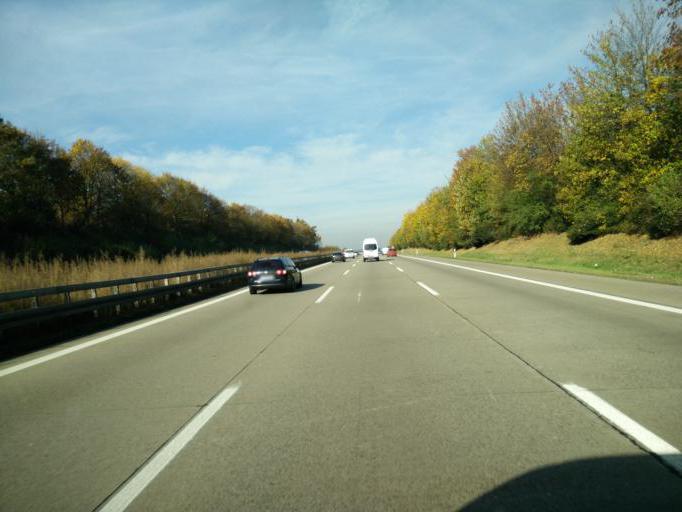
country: DE
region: Baden-Wuerttemberg
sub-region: Regierungsbezirk Stuttgart
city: Denkendorf
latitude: 48.6804
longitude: 9.3345
